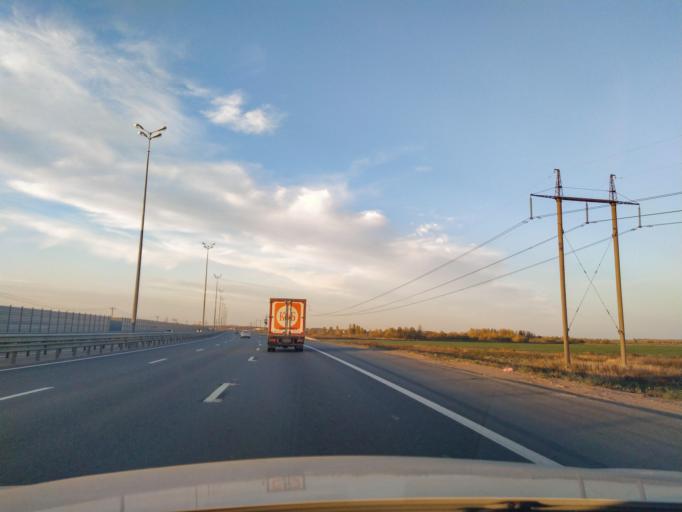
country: RU
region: Leningrad
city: Maloye Verevo
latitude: 59.5857
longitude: 30.1814
